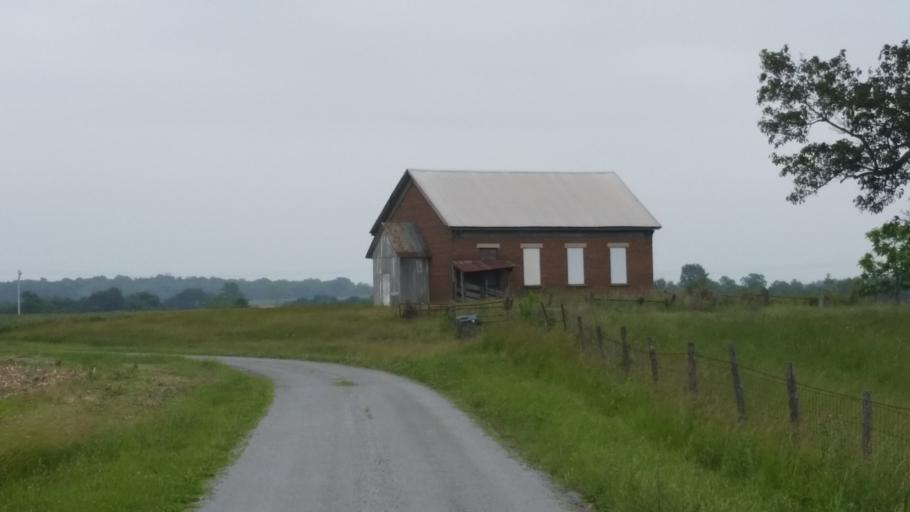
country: US
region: Ohio
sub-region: Highland County
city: Hillsboro
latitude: 39.2345
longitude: -83.4917
